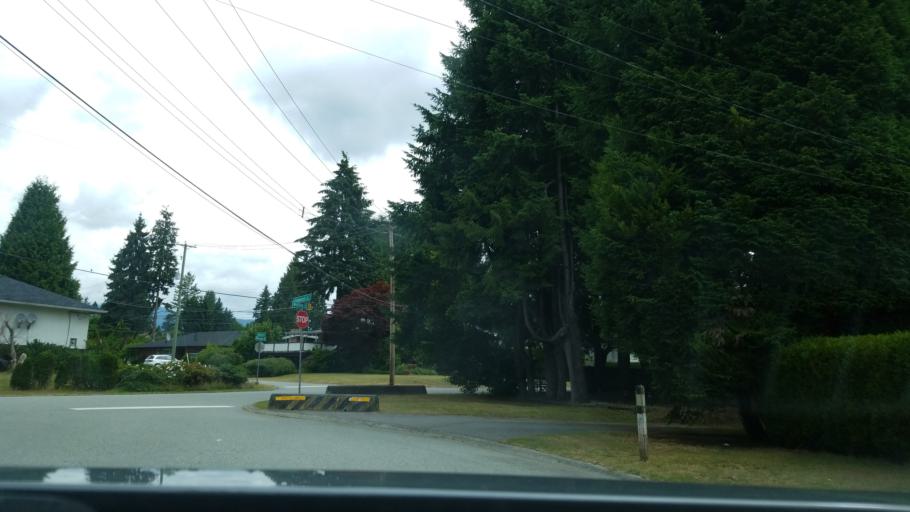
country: CA
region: British Columbia
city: Port Moody
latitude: 49.2655
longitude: -122.8867
